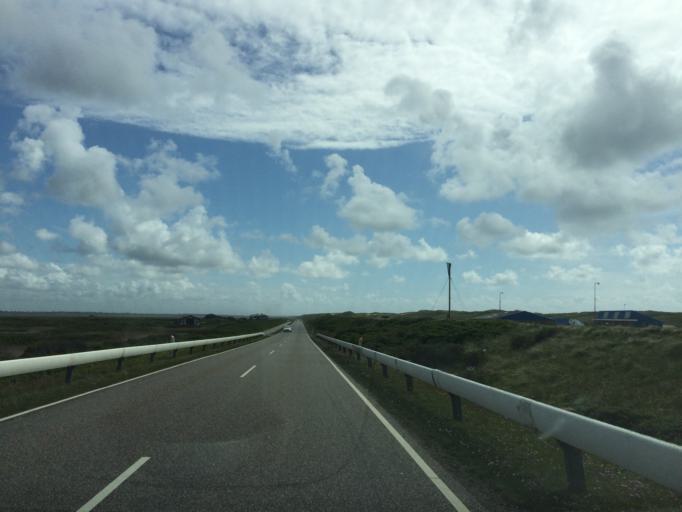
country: DK
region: Central Jutland
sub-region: Holstebro Kommune
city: Ulfborg
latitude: 56.3668
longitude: 8.1226
